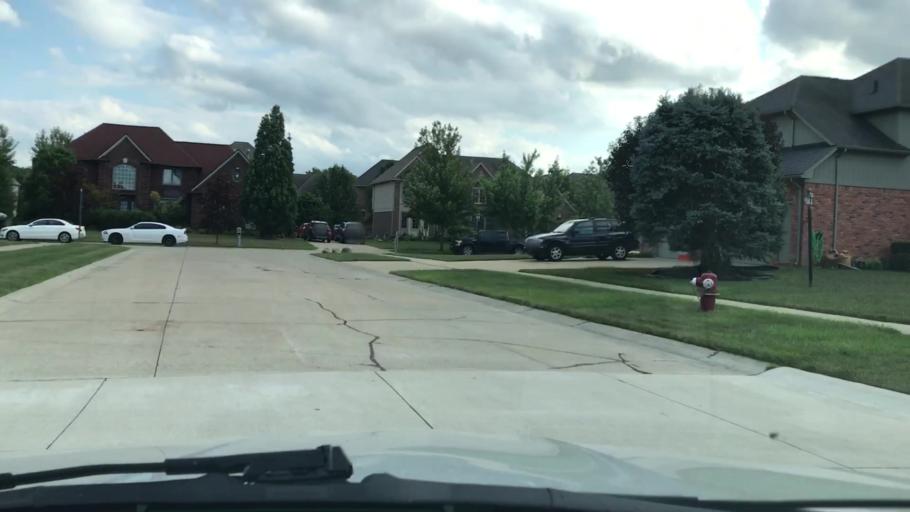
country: US
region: Michigan
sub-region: Macomb County
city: Utica
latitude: 42.6052
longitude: -83.0865
